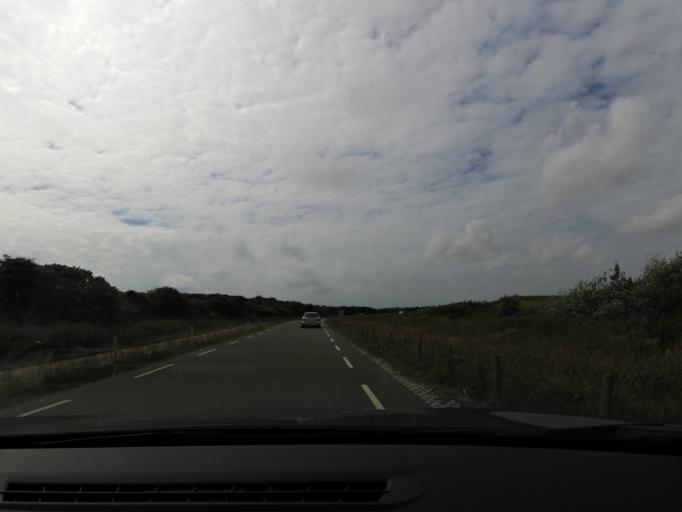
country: NL
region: Zeeland
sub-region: Gemeente Vlissingen
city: Vlissingen
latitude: 51.5069
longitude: 3.4703
